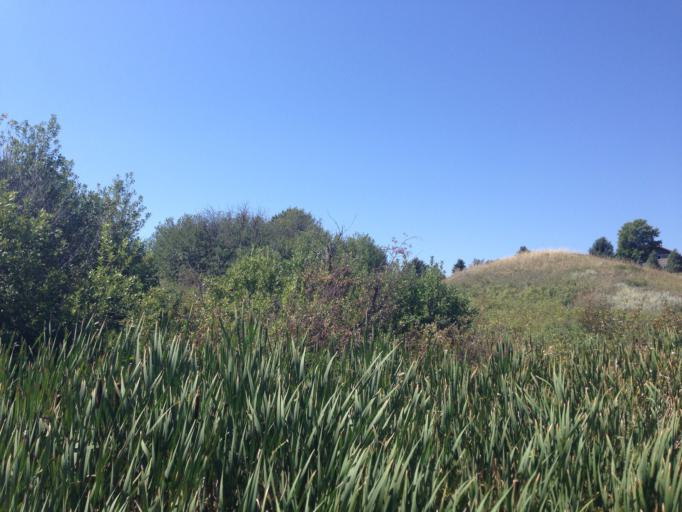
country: CA
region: Alberta
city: Medicine Hat
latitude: 50.0165
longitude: -110.6286
